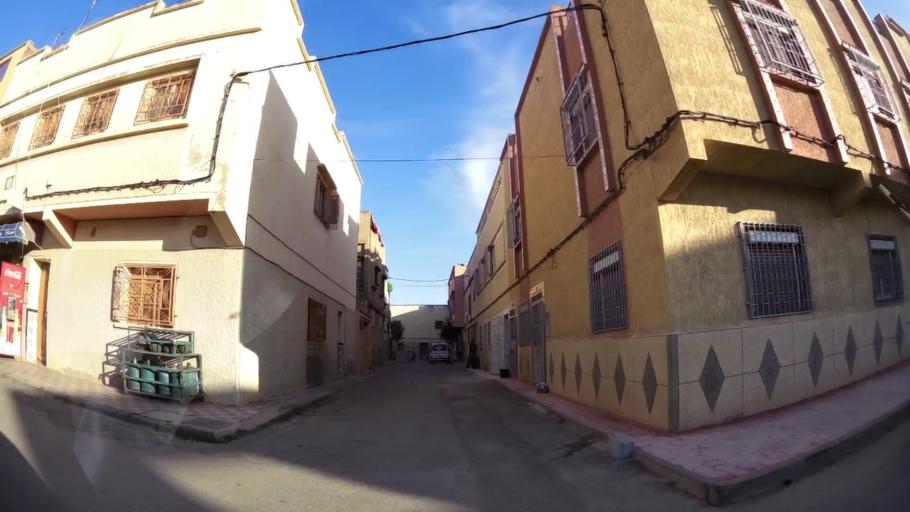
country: MA
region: Oriental
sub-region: Oujda-Angad
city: Oujda
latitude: 34.6981
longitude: -1.9041
